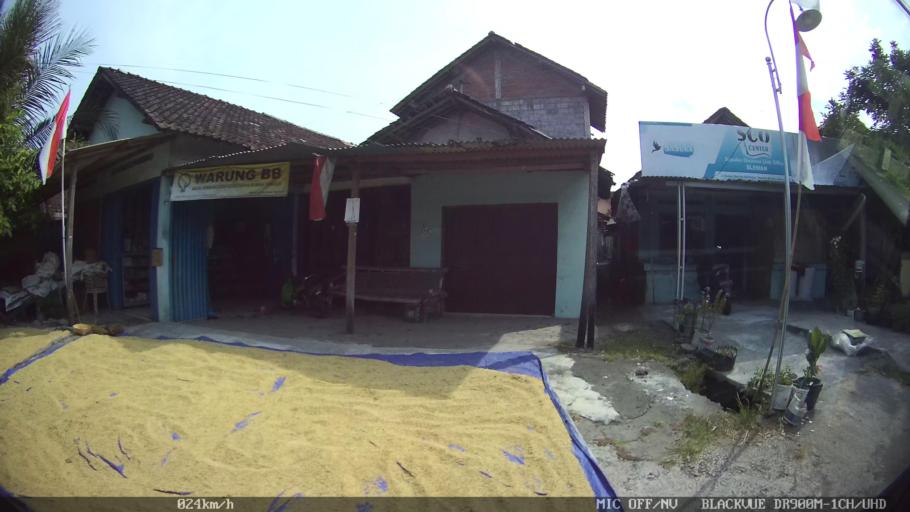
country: ID
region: Daerah Istimewa Yogyakarta
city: Depok
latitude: -7.8026
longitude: 110.4455
